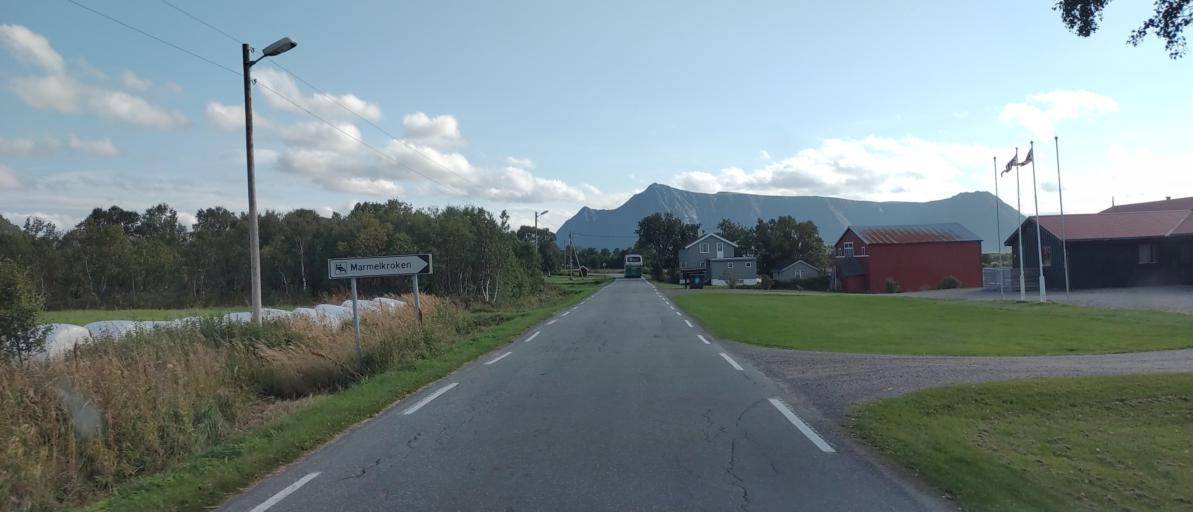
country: NO
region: Nordland
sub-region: Sortland
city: Sortland
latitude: 69.0415
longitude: 15.5157
